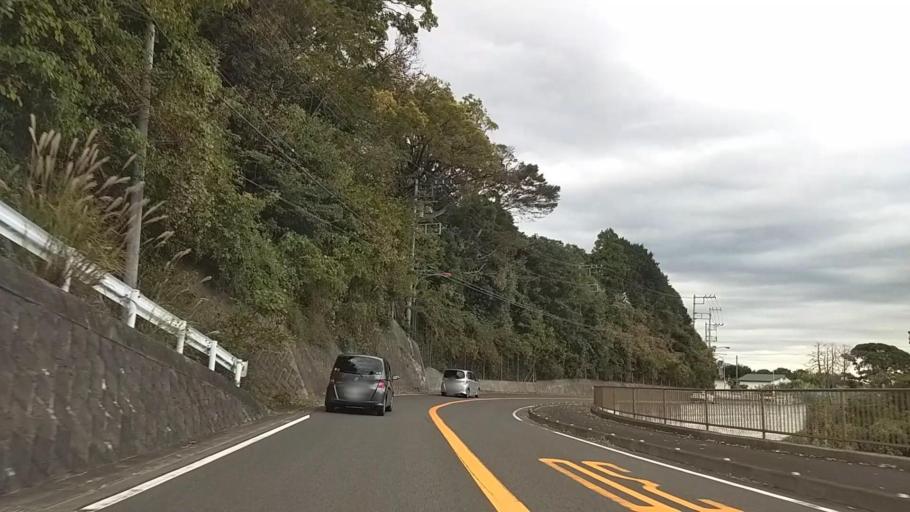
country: JP
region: Kanagawa
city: Odawara
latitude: 35.1950
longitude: 139.1341
